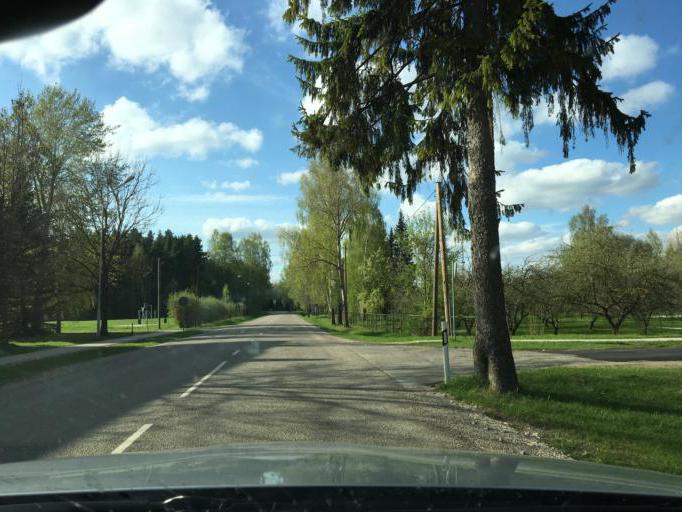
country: LV
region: Ozolnieku
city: Ozolnieki
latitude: 56.6836
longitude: 23.8350
